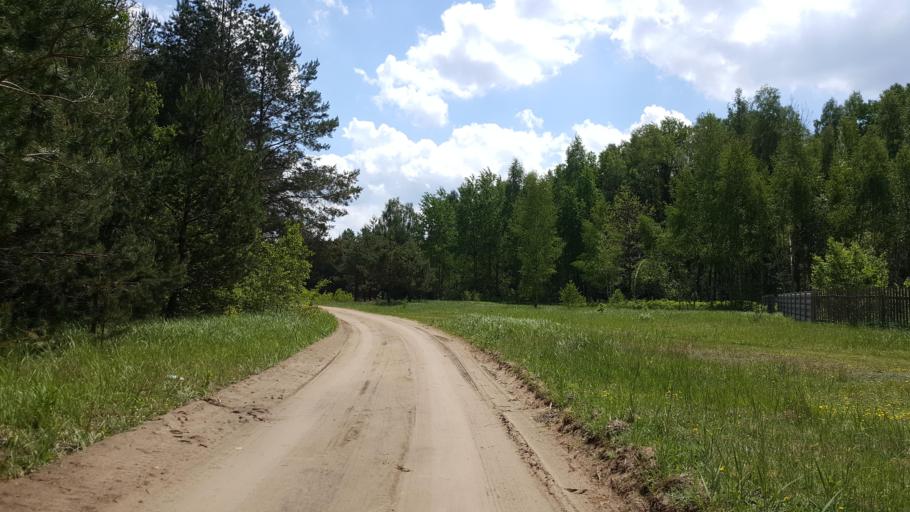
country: BY
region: Brest
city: Kamyanyuki
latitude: 52.4899
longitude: 23.9621
